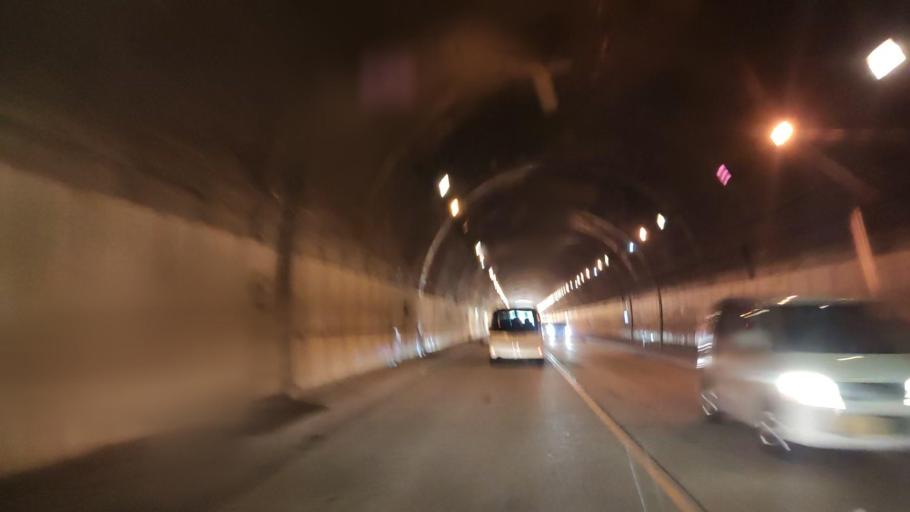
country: JP
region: Aomori
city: Aomori Shi
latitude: 40.8586
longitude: 140.8422
